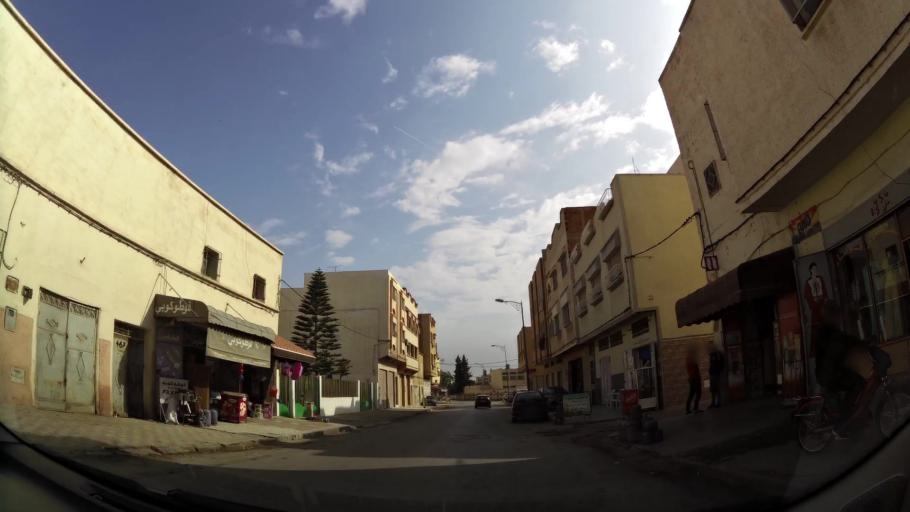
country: MA
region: Oriental
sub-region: Oujda-Angad
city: Oujda
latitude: 34.6935
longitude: -1.9034
